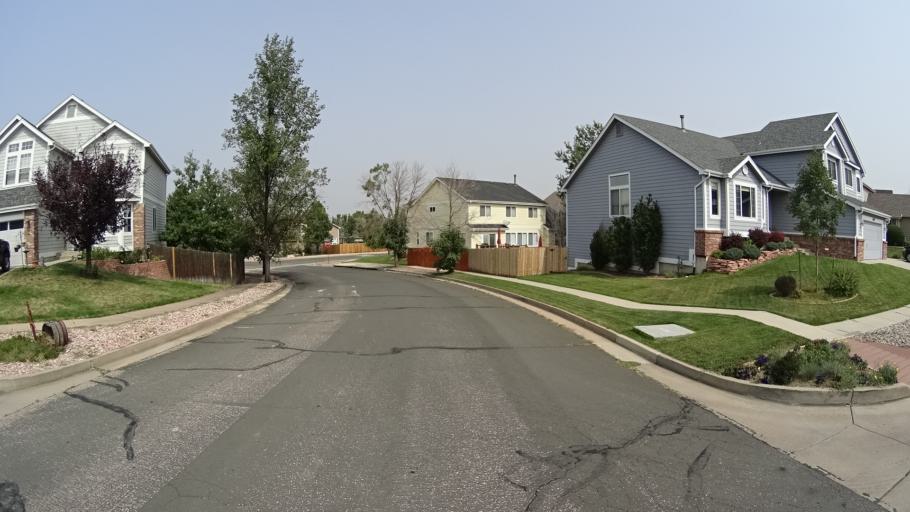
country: US
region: Colorado
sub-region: El Paso County
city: Cimarron Hills
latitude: 38.9187
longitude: -104.7508
